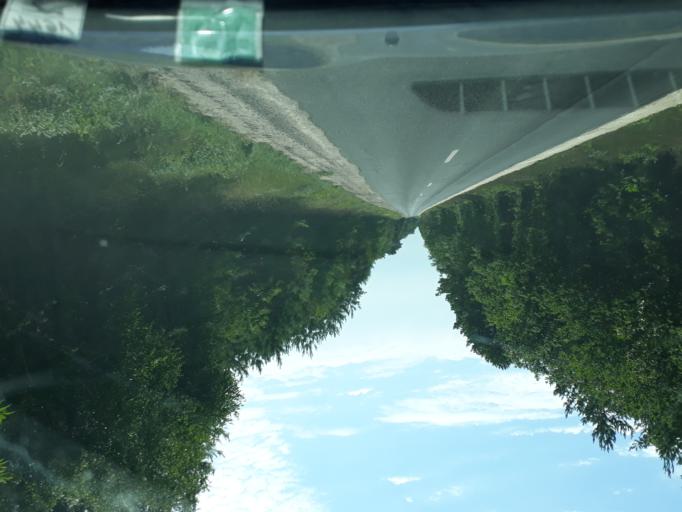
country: FR
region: Centre
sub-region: Departement du Loir-et-Cher
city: Vouzon
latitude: 47.6464
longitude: 2.0366
